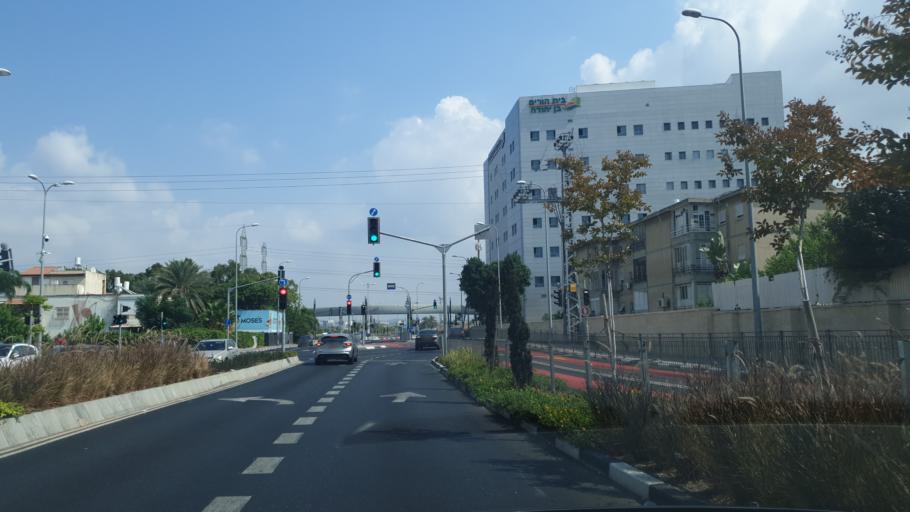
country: IL
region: Haifa
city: Qiryat Bialik
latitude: 32.8170
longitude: 35.0785
